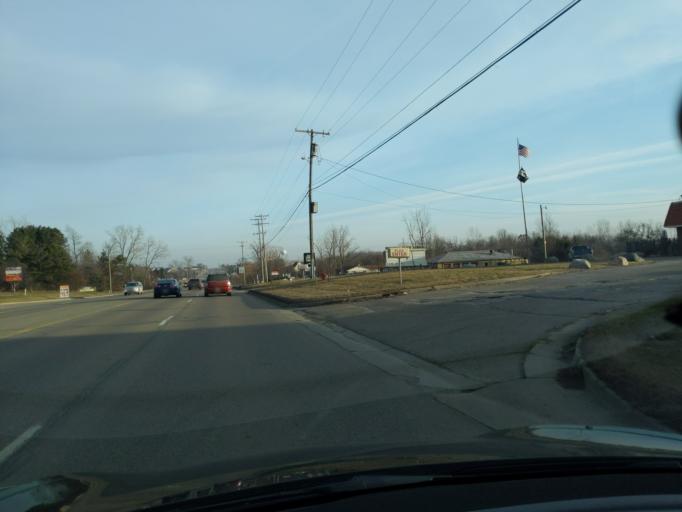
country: US
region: Michigan
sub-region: Livingston County
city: Howell
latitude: 42.5956
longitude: -83.8986
